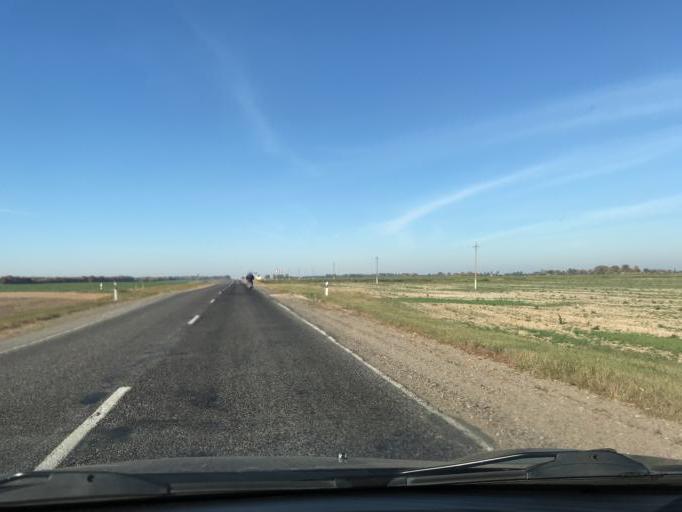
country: BY
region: Gomel
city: Brahin
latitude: 51.7913
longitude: 30.1746
